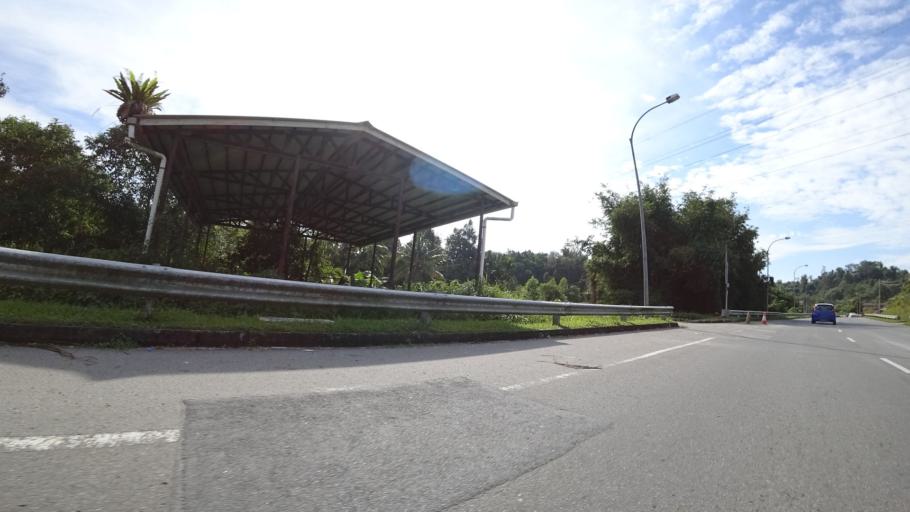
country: BN
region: Brunei and Muara
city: Bandar Seri Begawan
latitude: 4.8753
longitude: 114.8045
